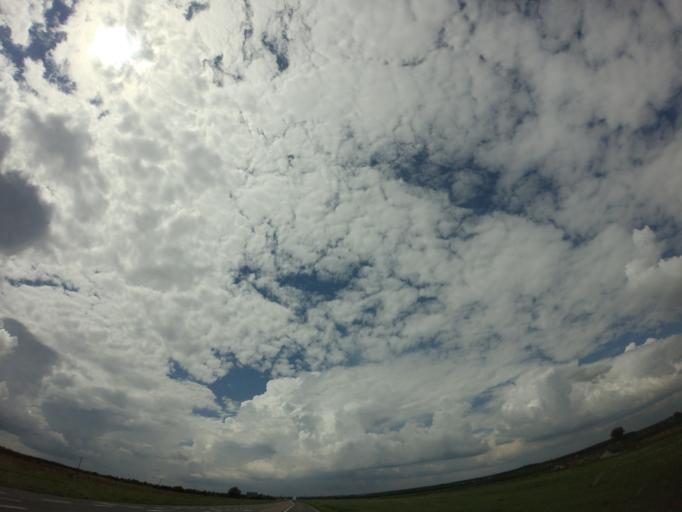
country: PL
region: Lublin Voivodeship
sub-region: Powiat opolski
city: Laziska
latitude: 51.1296
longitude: 21.8827
